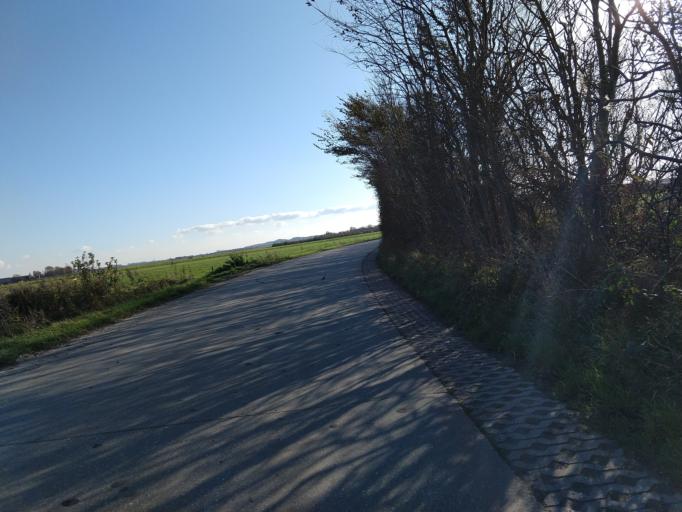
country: NL
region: Zeeland
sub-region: Gemeente Vlissingen
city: Vlissingen
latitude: 51.5343
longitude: 3.4801
